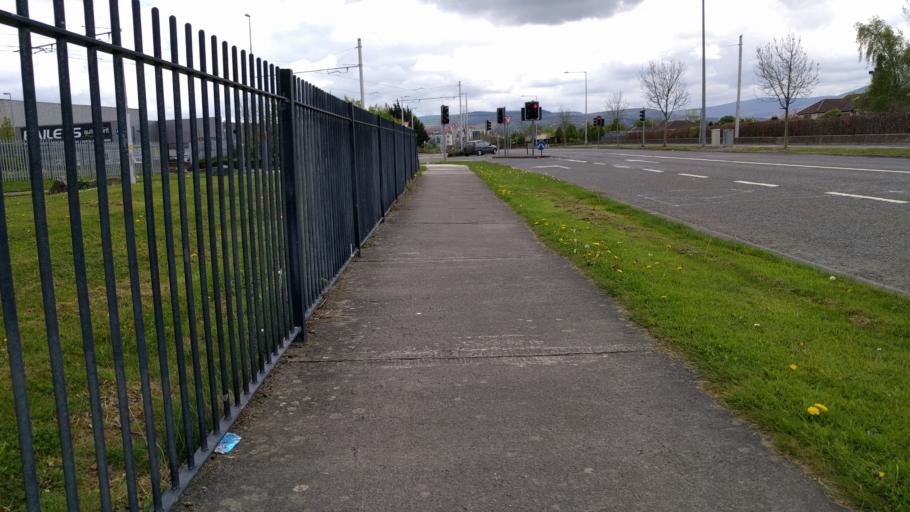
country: IE
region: Leinster
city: Tallaght
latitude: 53.2944
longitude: -6.3857
